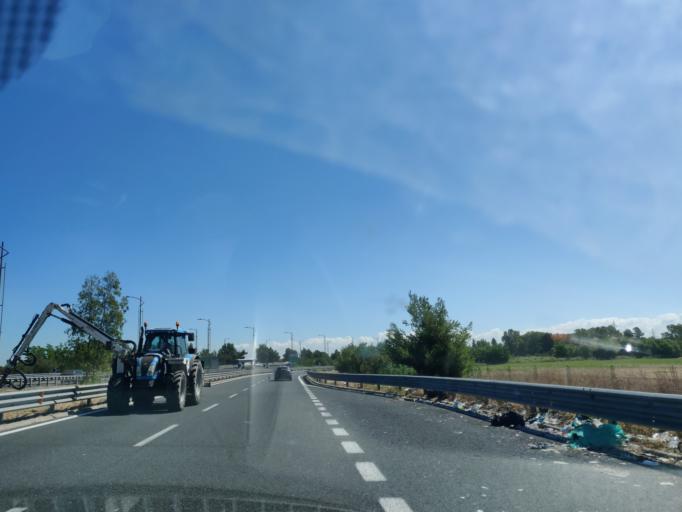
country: IT
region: Latium
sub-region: Citta metropolitana di Roma Capitale
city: Npp 23 (Parco Leonardo)
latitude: 41.8103
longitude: 12.3147
